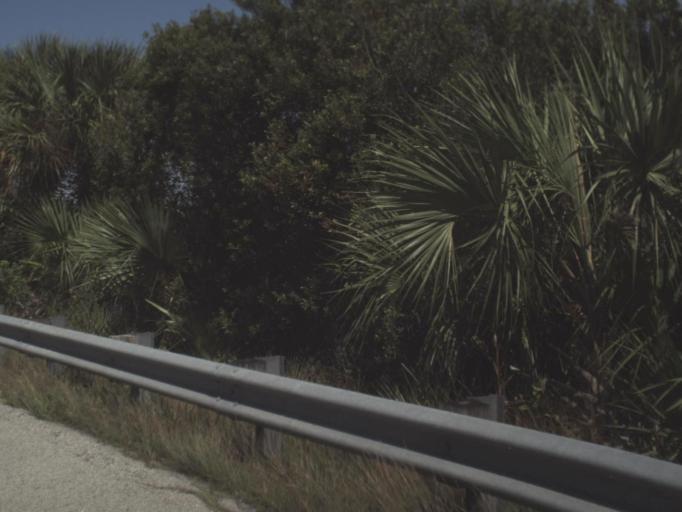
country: US
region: Florida
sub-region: Collier County
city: Marco
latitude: 25.9454
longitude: -81.4763
